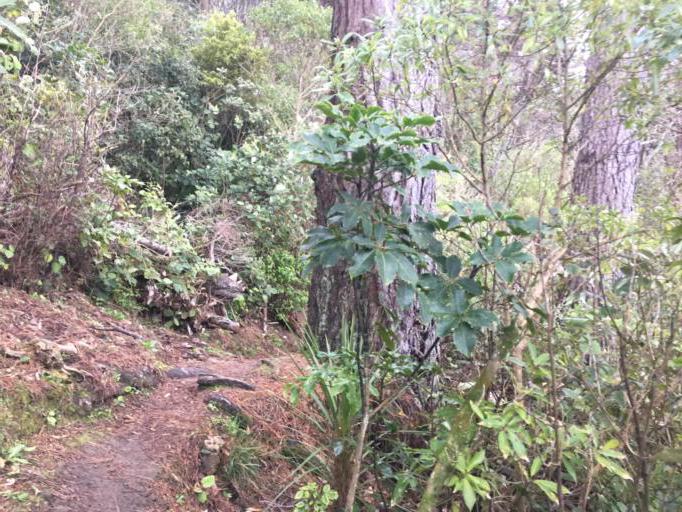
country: NZ
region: Wellington
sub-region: Wellington City
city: Kelburn
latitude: -41.2761
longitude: 174.7670
